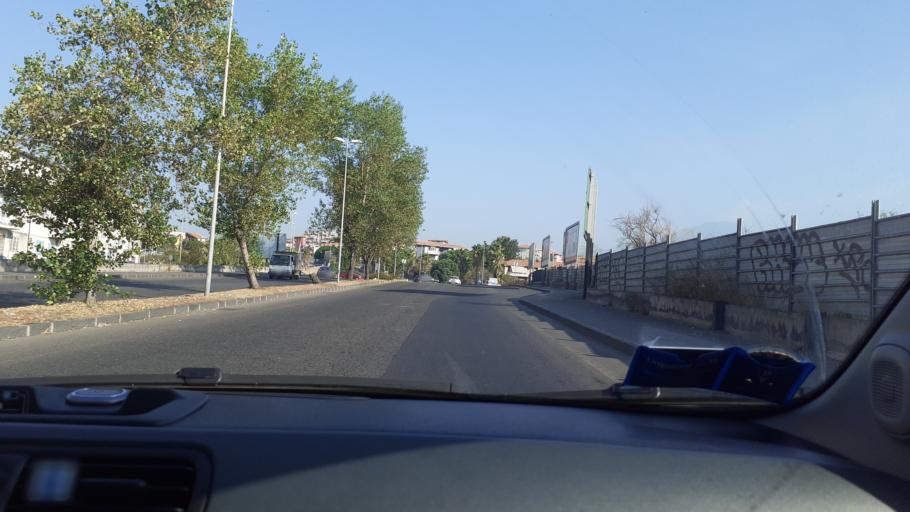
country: IT
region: Sicily
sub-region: Catania
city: Misterbianco
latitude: 37.5155
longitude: 15.0529
